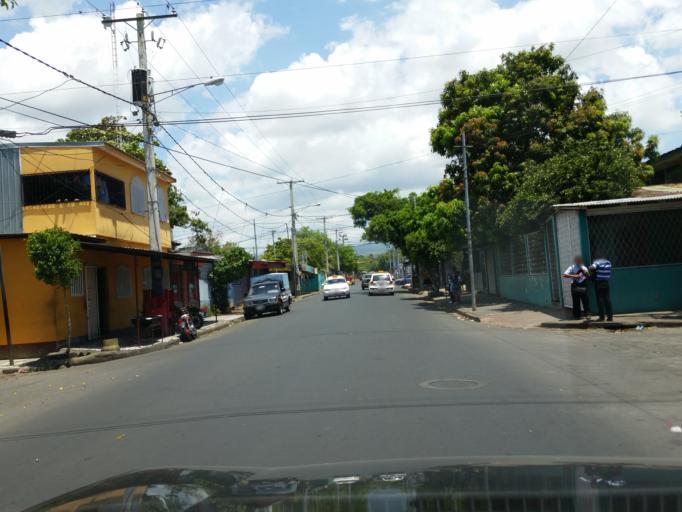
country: NI
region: Managua
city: Managua
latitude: 12.1379
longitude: -86.2537
